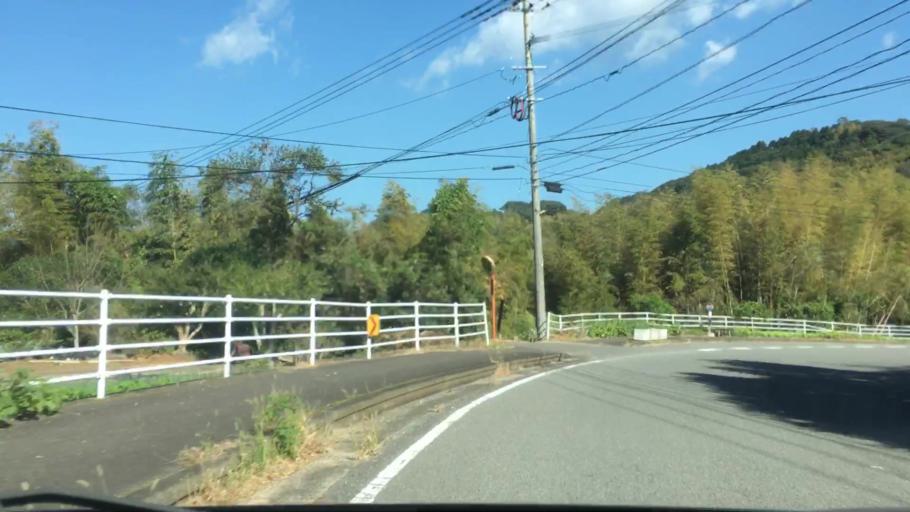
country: JP
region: Nagasaki
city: Sasebo
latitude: 33.0125
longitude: 129.6541
